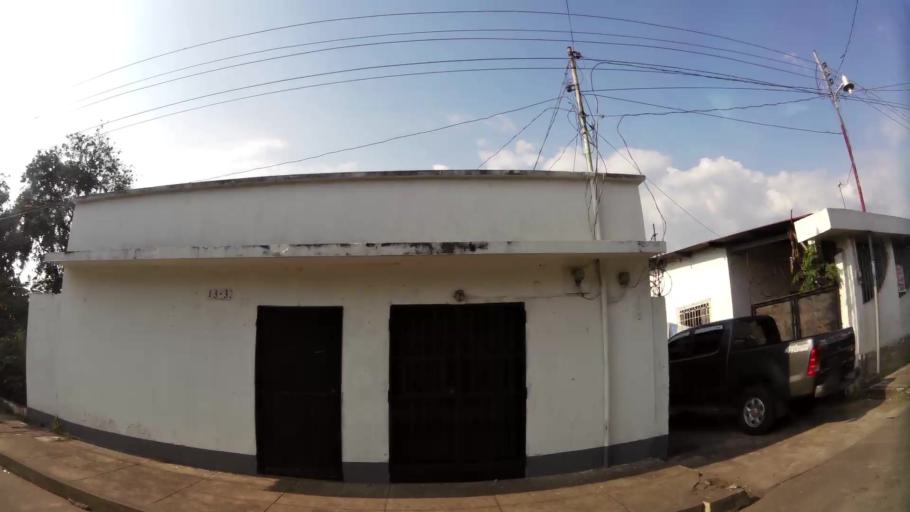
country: GT
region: Retalhuleu
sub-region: Municipio de Retalhuleu
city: Retalhuleu
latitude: 14.5299
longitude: -91.6911
